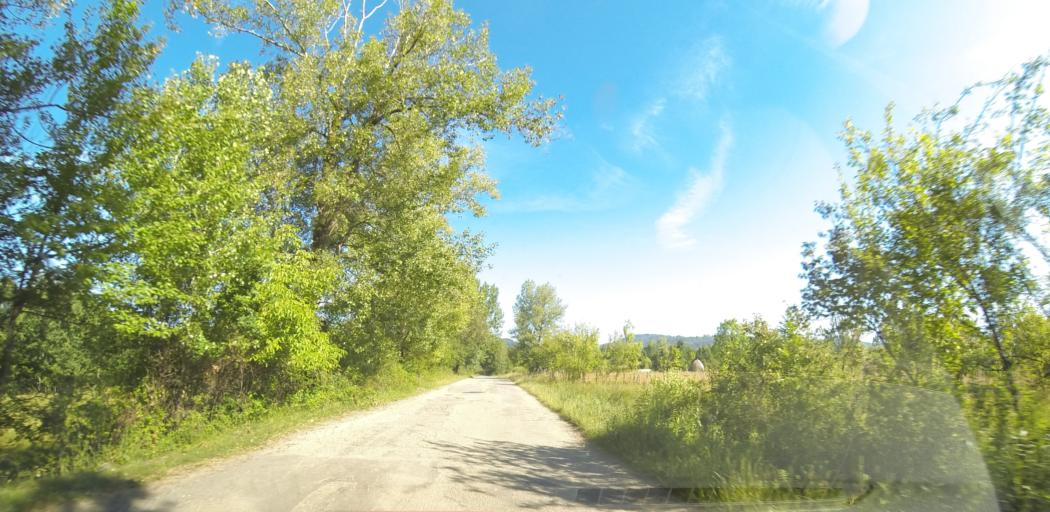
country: RO
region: Gorj
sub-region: Comuna Polovragi
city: Polovragi
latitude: 45.1715
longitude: 23.8555
